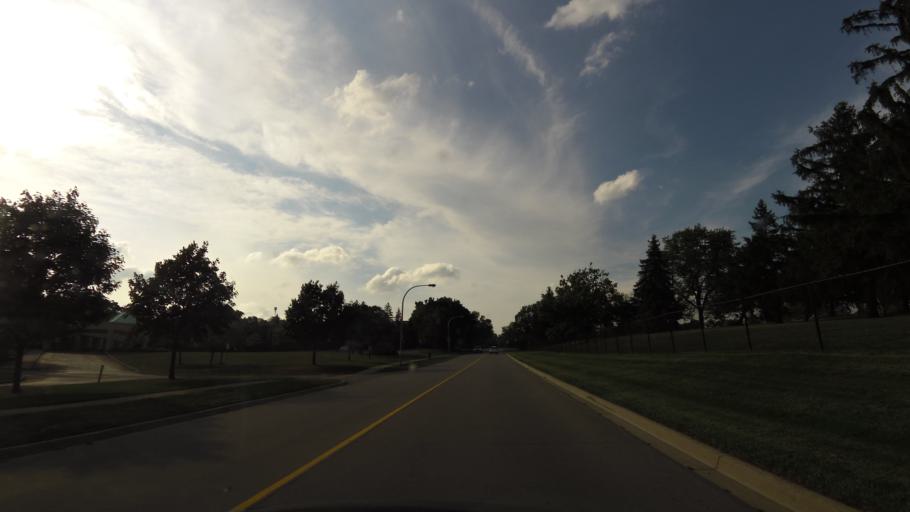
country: CA
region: Ontario
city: Burlington
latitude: 43.3387
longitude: -79.8347
